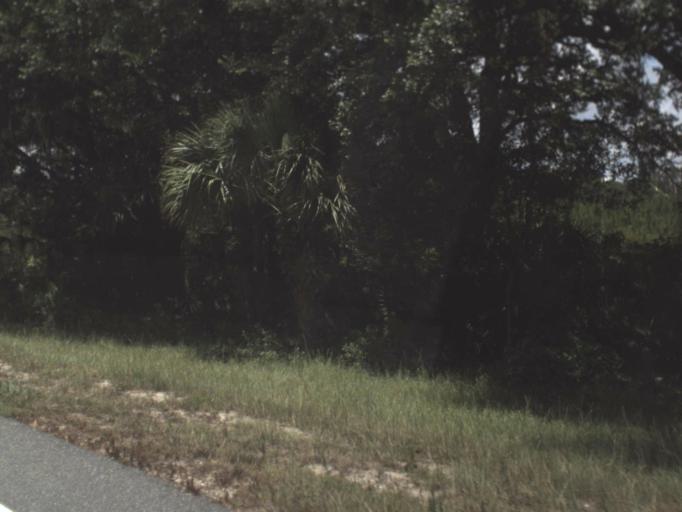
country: US
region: Florida
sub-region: Taylor County
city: Perry
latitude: 30.1419
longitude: -83.8689
